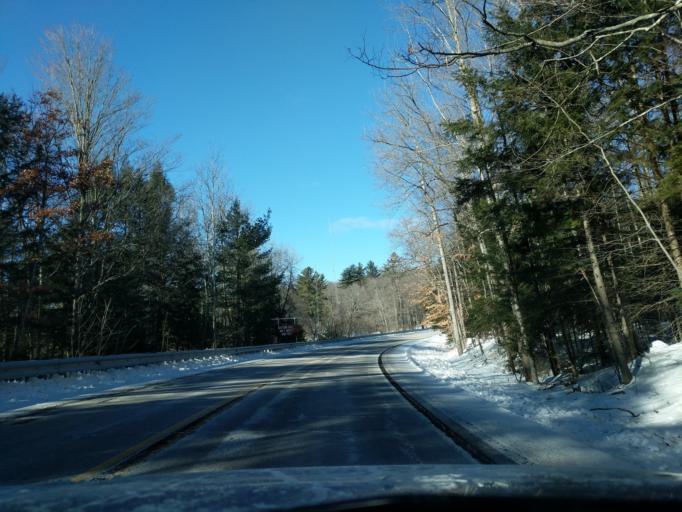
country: US
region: Wisconsin
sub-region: Menominee County
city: Keshena
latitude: 45.0933
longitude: -88.6336
